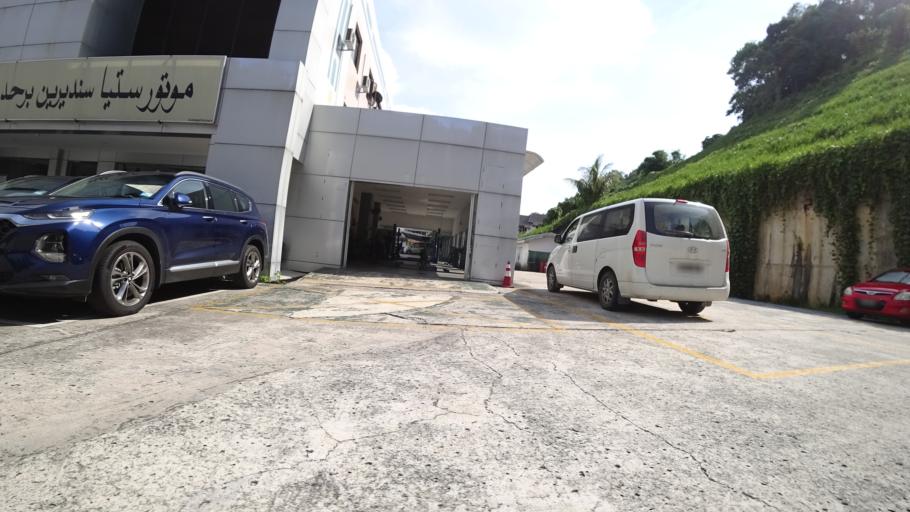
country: BN
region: Brunei and Muara
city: Bandar Seri Begawan
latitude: 4.8606
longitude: 114.8954
